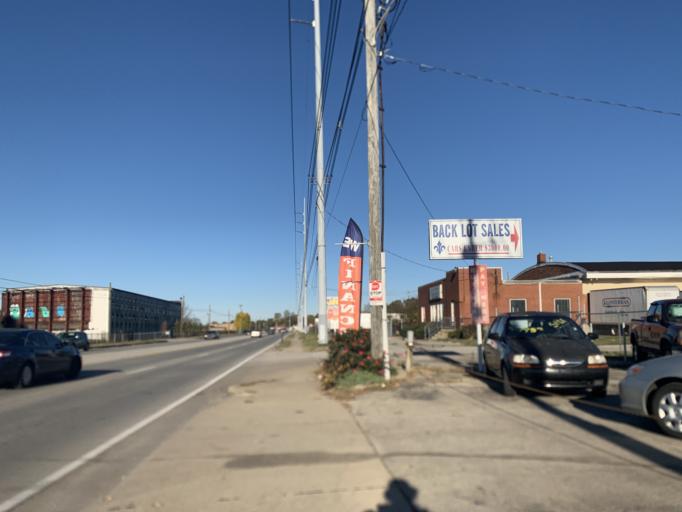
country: US
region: Kentucky
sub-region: Jefferson County
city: Shively
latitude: 38.1999
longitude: -85.7955
